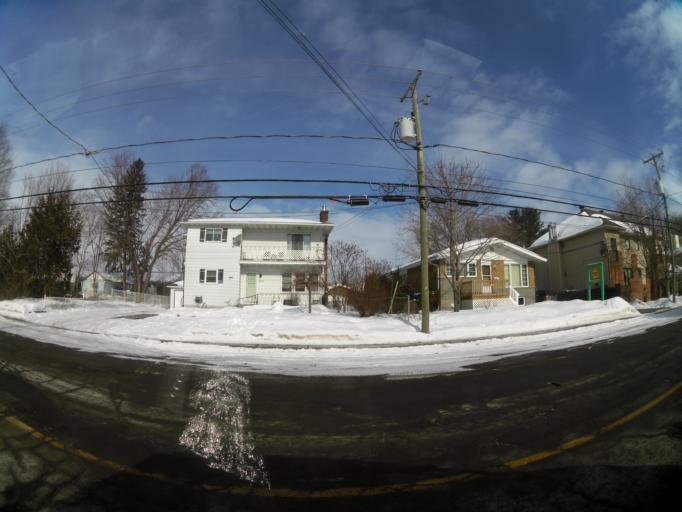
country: CA
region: Quebec
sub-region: Outaouais
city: Gatineau
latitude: 45.4810
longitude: -75.6279
